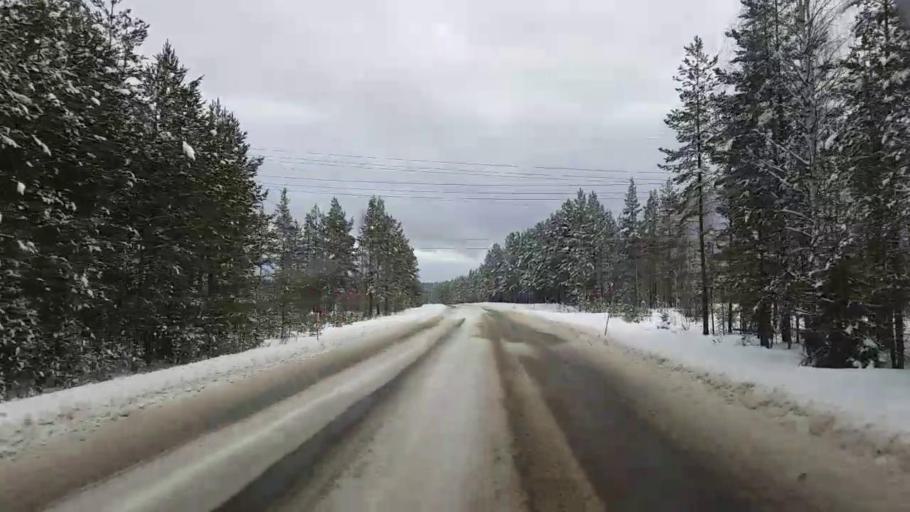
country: SE
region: Vaesternorrland
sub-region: Ange Kommun
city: Ange
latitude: 62.0676
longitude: 15.1061
